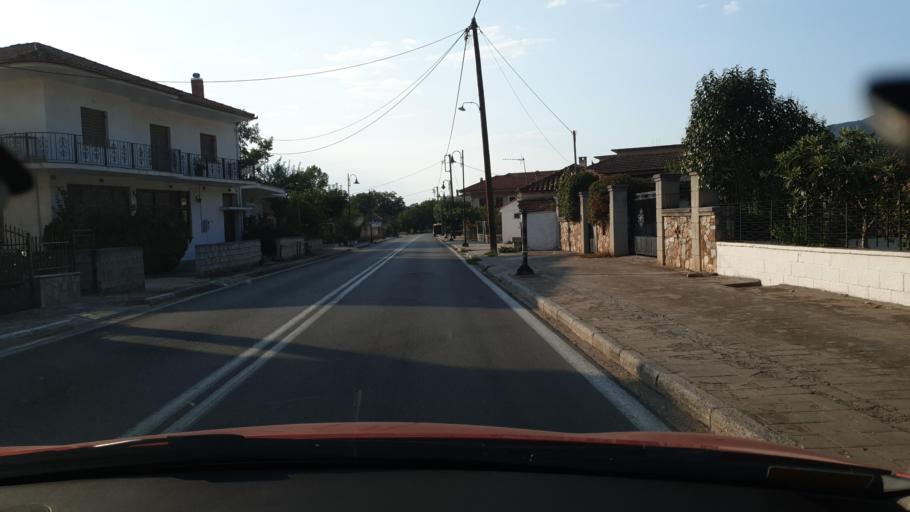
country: GR
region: Thessaly
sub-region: Nomos Magnisias
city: Sourpi
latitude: 39.0999
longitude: 22.8961
